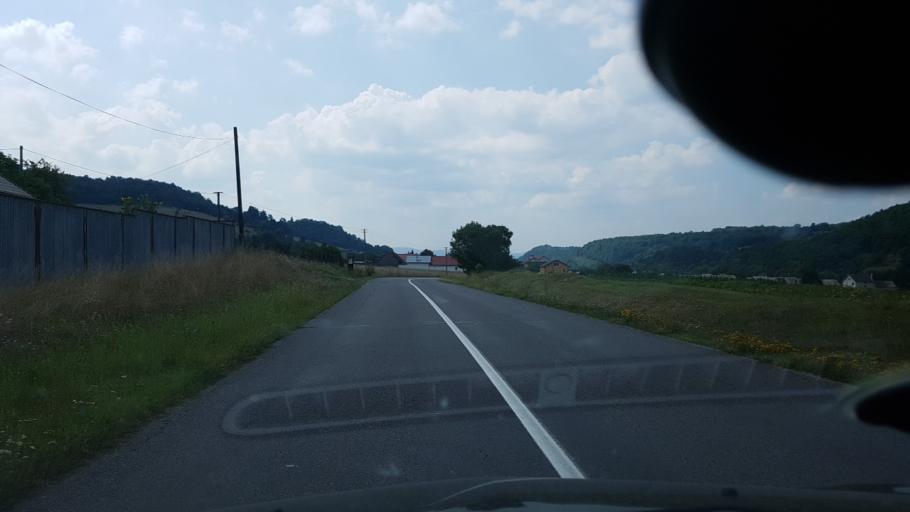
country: SK
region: Banskobystricky
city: Hrochot,Slovakia
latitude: 48.6538
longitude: 19.2448
